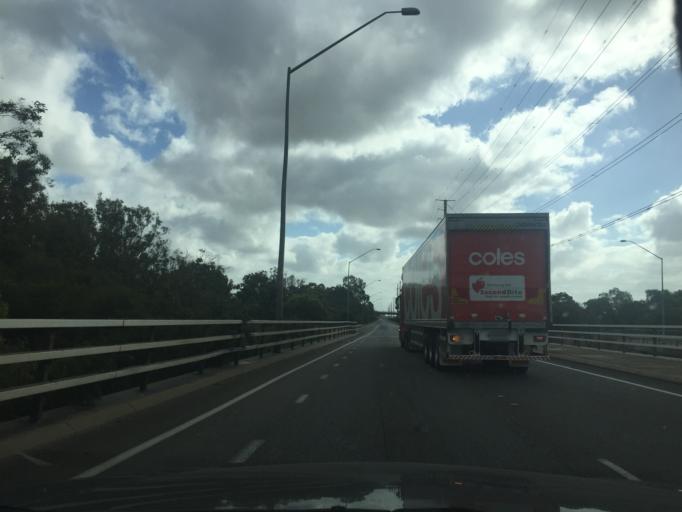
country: AU
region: Western Australia
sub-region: Gosnells
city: Kenwick
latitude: -32.0401
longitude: 115.9554
